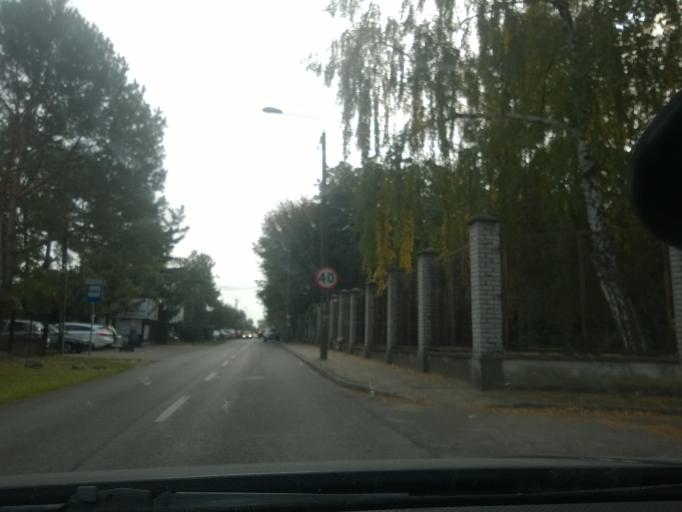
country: PL
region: Masovian Voivodeship
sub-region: Powiat pruszkowski
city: Pruszkow
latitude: 52.1704
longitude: 20.8293
